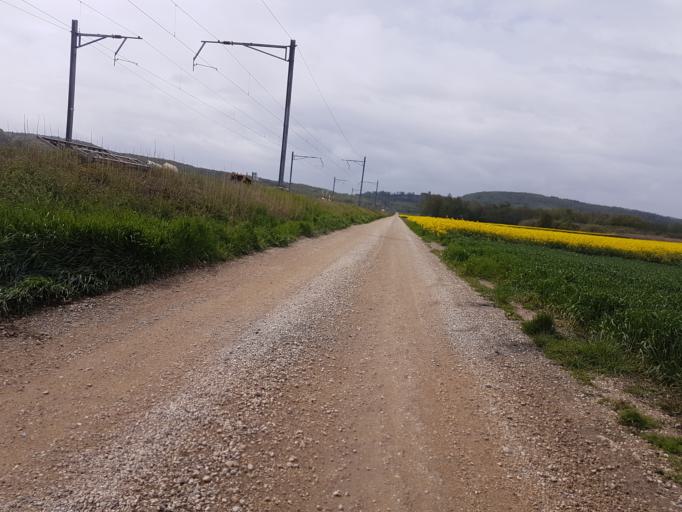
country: CH
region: Vaud
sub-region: Jura-Nord vaudois District
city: Bavois
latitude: 46.6811
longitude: 6.5567
